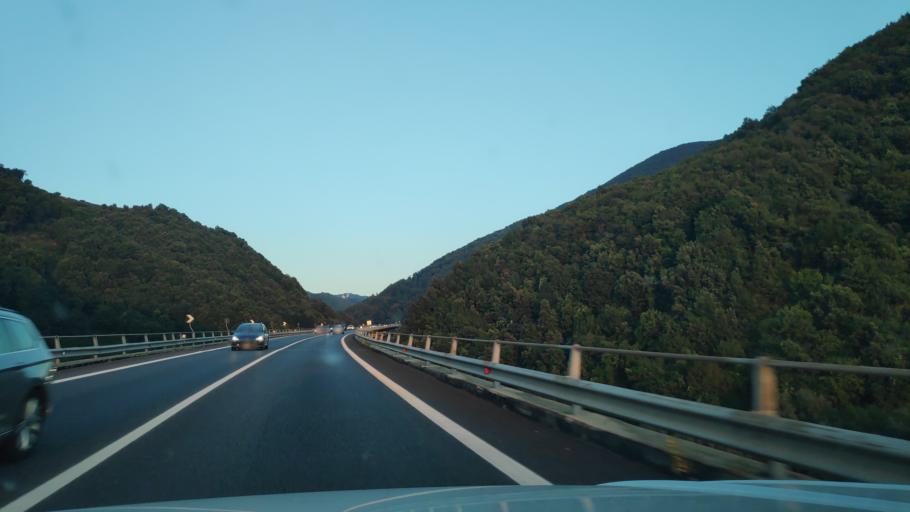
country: IT
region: Calabria
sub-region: Provincia di Reggio Calabria
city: Anoia Superiore
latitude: 38.4170
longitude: 16.1242
